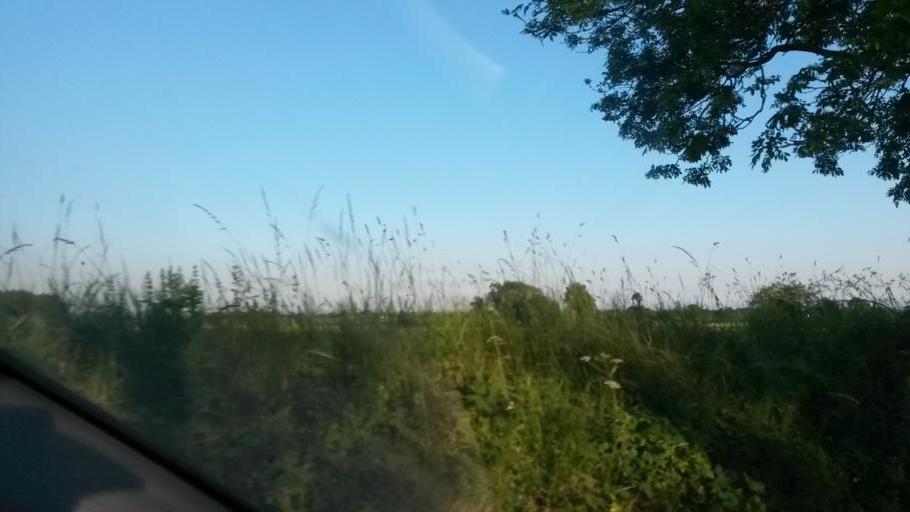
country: IE
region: Leinster
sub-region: An Mhi
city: Ashbourne
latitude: 53.5463
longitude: -6.3597
